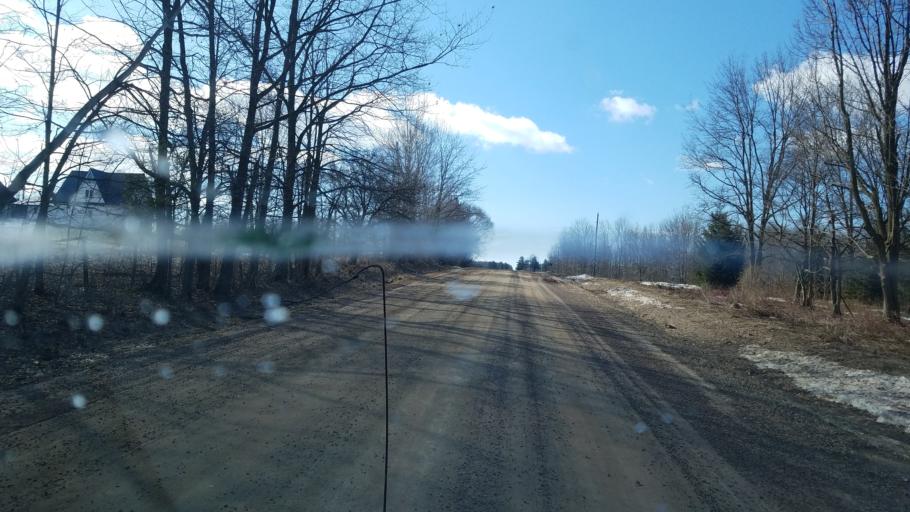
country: US
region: Wisconsin
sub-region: Clark County
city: Loyal
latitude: 44.6744
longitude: -90.4559
